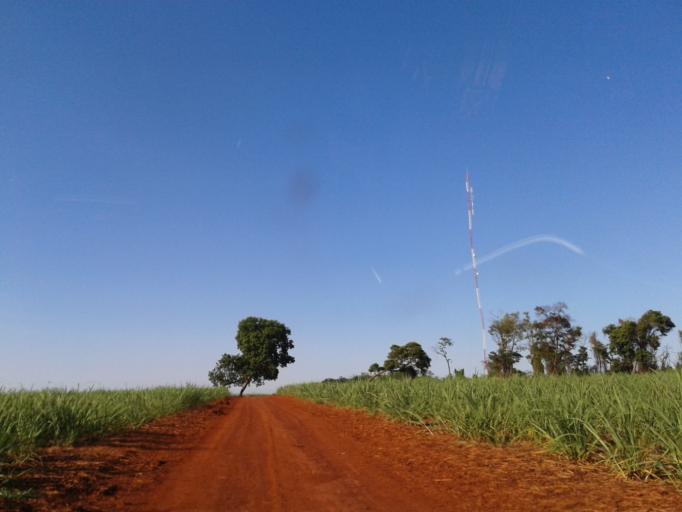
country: BR
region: Minas Gerais
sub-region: Centralina
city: Centralina
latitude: -18.6670
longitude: -49.2603
